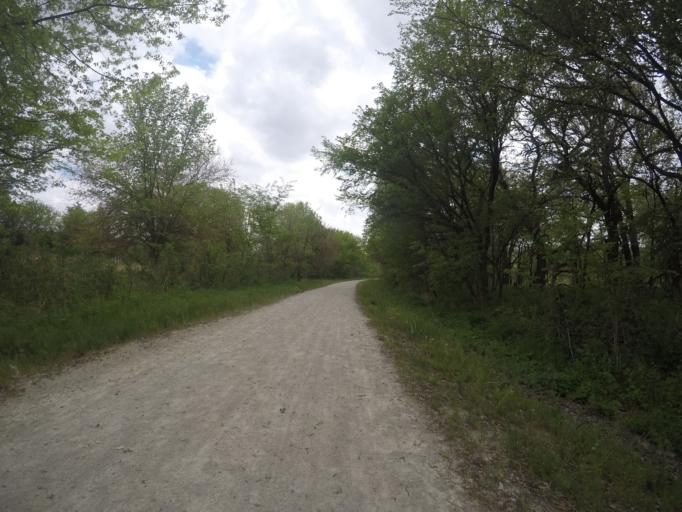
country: US
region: Kansas
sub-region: Marshall County
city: Marysville
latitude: 39.8716
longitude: -96.6436
